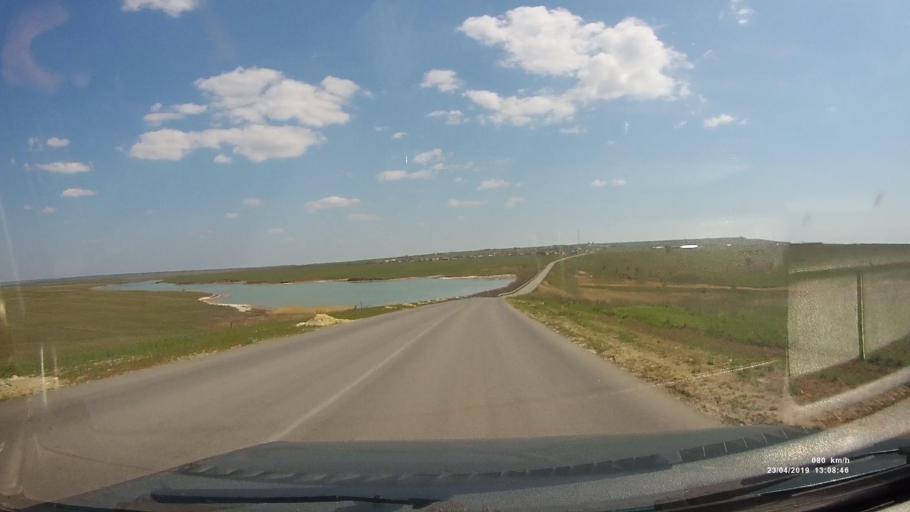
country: RU
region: Kalmykiya
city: Yashalta
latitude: 46.5804
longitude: 42.7801
